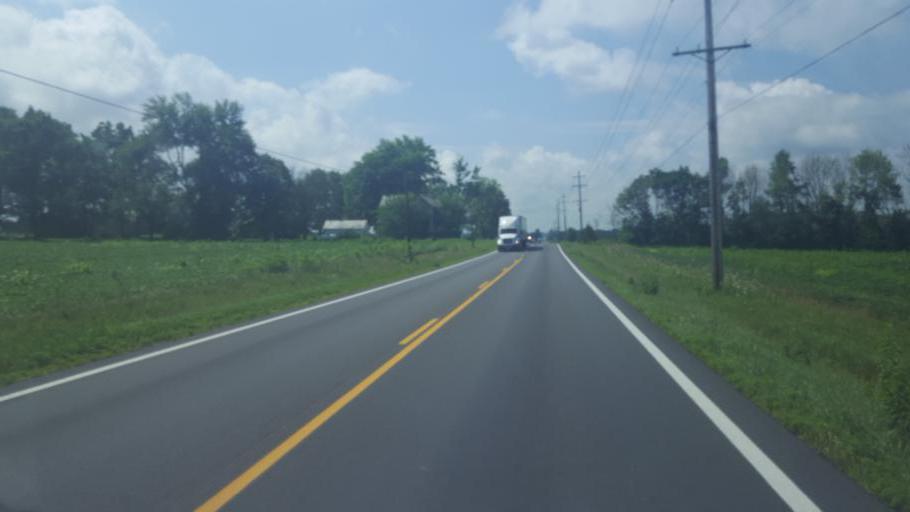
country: US
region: Ohio
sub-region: Fairfield County
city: Baltimore
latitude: 39.8370
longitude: -82.5688
